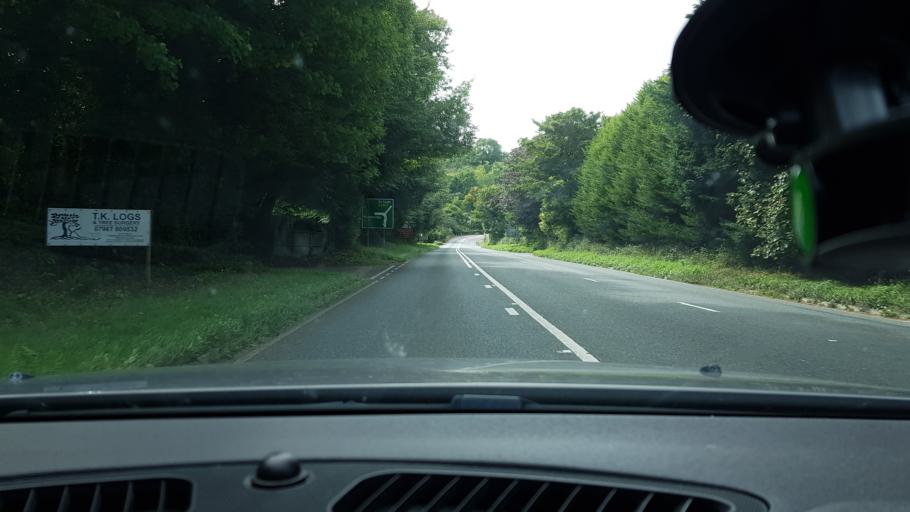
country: GB
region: England
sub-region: Cornwall
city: Camelford
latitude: 50.5942
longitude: -4.7240
